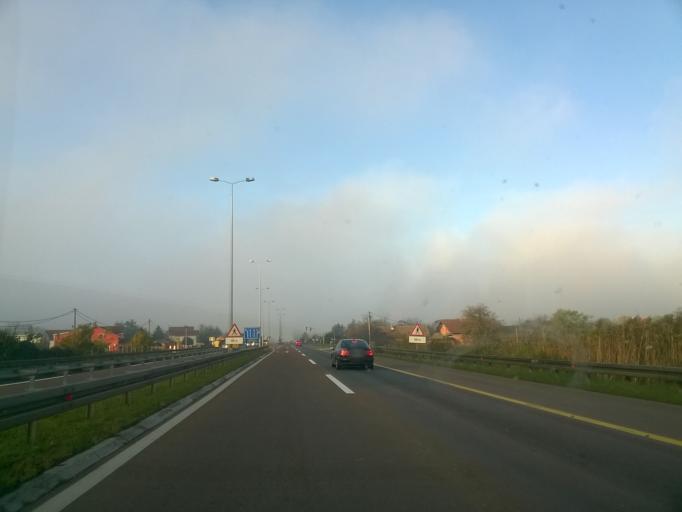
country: RS
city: Ovca
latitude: 44.8595
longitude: 20.5636
